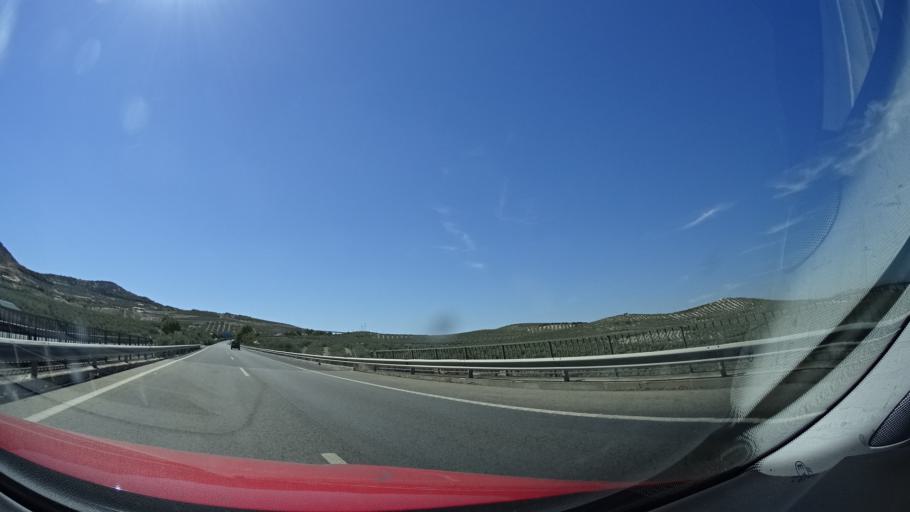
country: ES
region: Andalusia
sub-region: Provincia de Sevilla
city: Estepa
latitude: 37.2986
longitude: -4.8907
